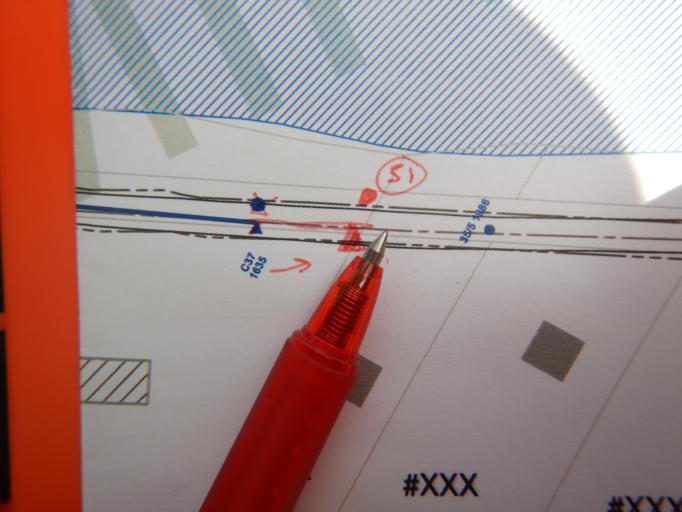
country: US
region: Florida
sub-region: Sarasota County
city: Vamo
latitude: 27.2265
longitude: -82.5207
